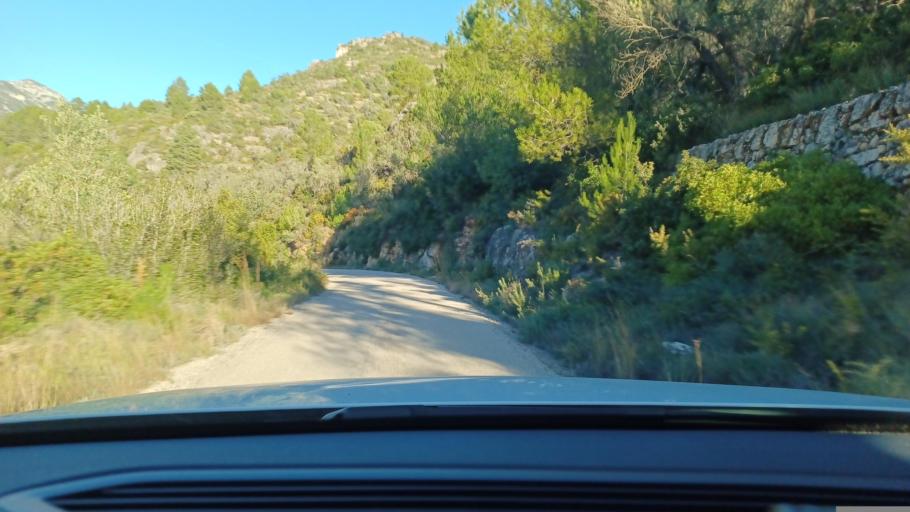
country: ES
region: Catalonia
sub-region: Provincia de Tarragona
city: Mas de Barberans
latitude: 40.7204
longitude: 0.3472
